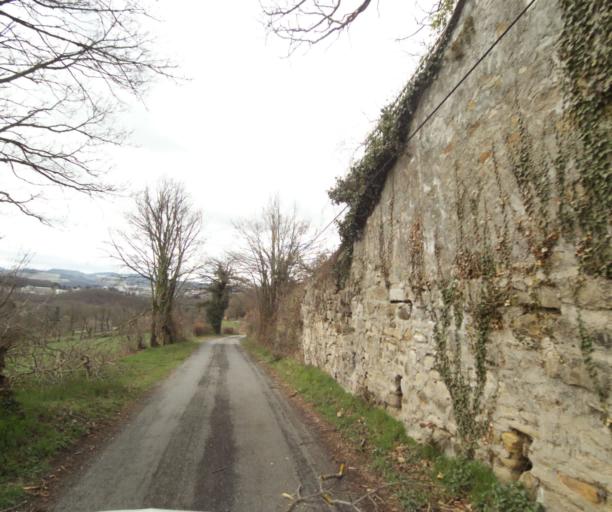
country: FR
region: Rhone-Alpes
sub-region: Departement de la Loire
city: La Talaudiere
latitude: 45.4836
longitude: 4.4115
